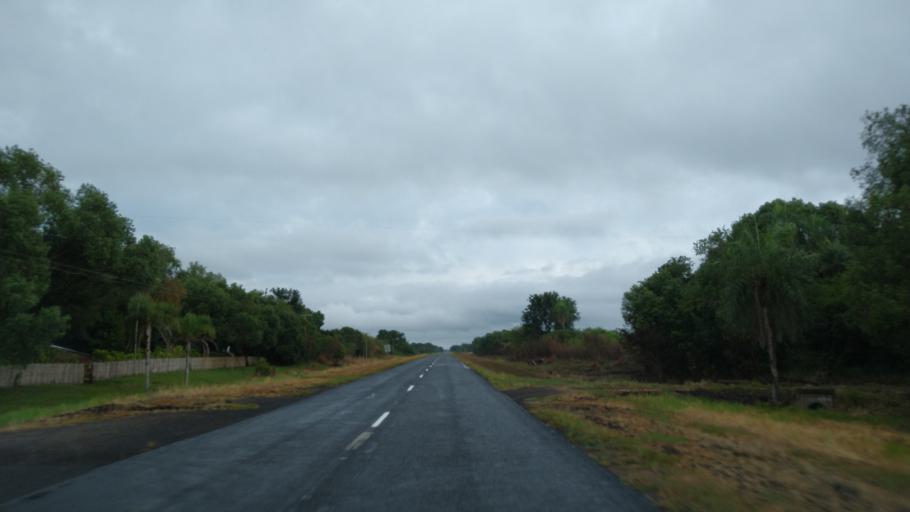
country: AR
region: Corrientes
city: Loreto
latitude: -27.7474
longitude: -57.2533
